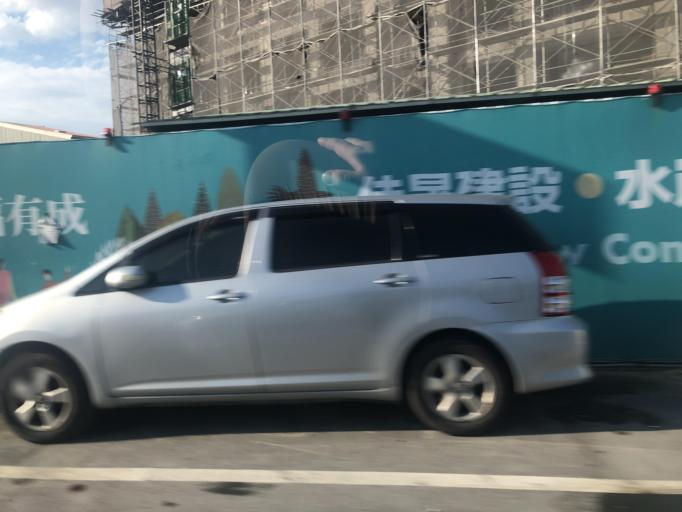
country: TW
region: Taiwan
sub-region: Tainan
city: Tainan
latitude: 23.0303
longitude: 120.1943
